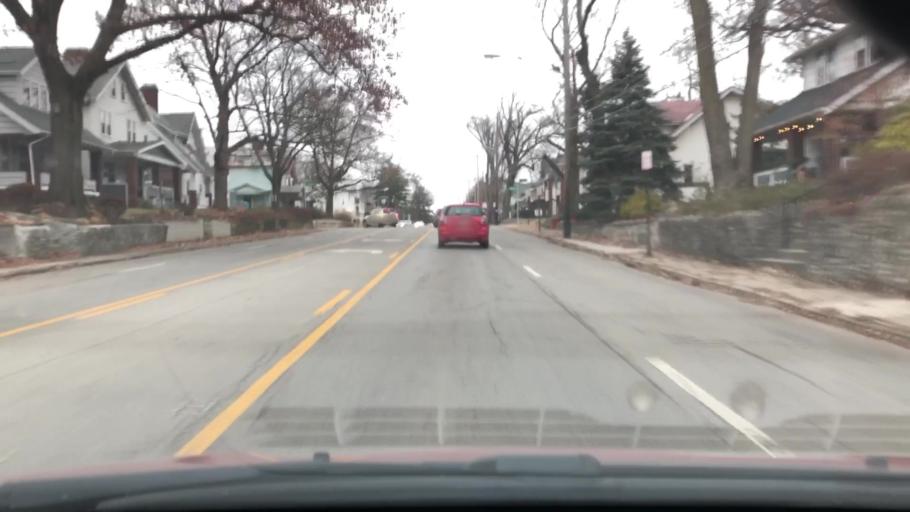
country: US
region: Ohio
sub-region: Franklin County
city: Grandview Heights
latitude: 40.0206
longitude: -83.0019
